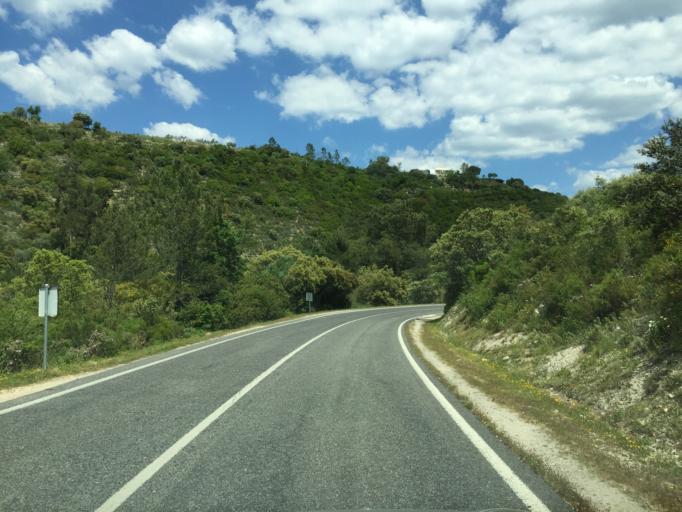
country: PT
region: Santarem
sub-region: Ourem
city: Fatima
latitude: 39.6418
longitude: -8.6349
